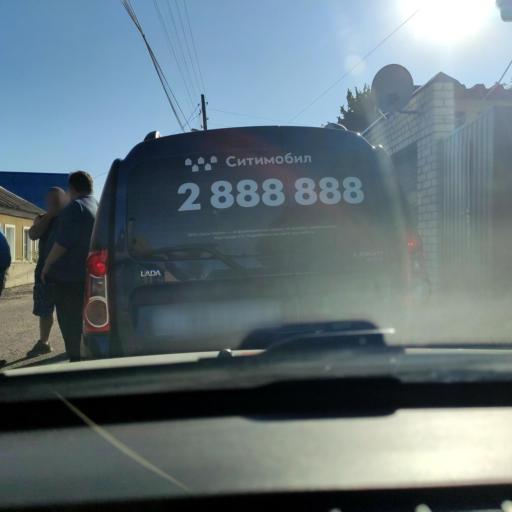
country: RU
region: Voronezj
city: Voronezh
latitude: 51.6325
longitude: 39.2018
